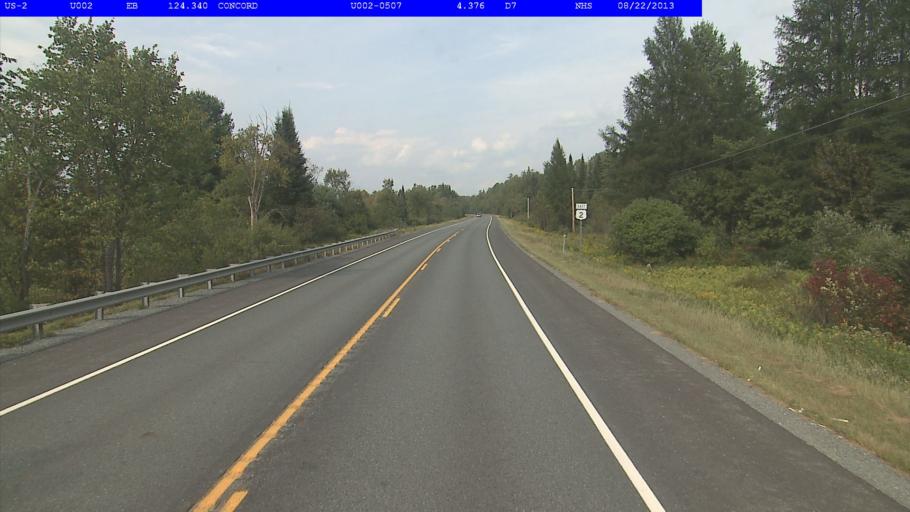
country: US
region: Vermont
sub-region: Caledonia County
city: St Johnsbury
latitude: 44.4555
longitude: -71.8681
